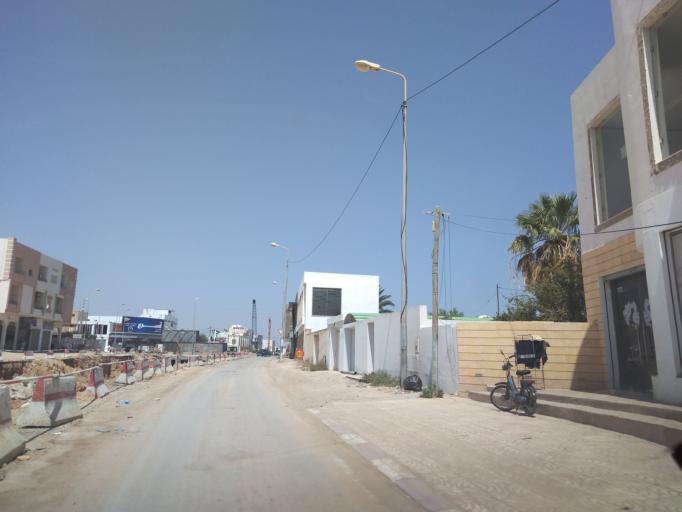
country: TN
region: Safaqis
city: Sfax
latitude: 34.7506
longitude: 10.7297
